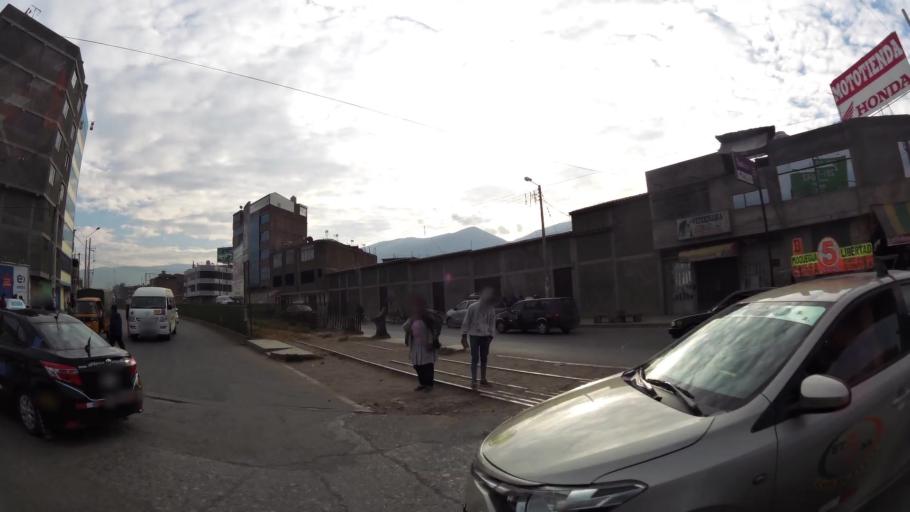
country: PE
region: Junin
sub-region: Provincia de Huancayo
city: Huancayo
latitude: -12.0765
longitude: -75.2055
